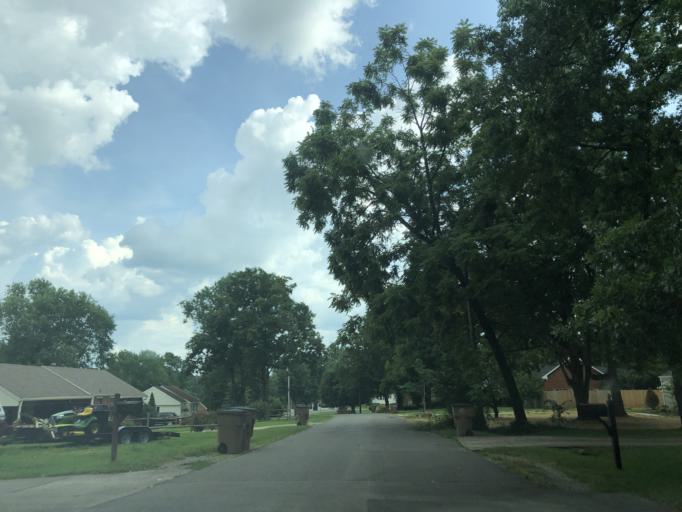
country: US
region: Tennessee
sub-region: Davidson County
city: Lakewood
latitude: 36.1633
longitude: -86.6797
